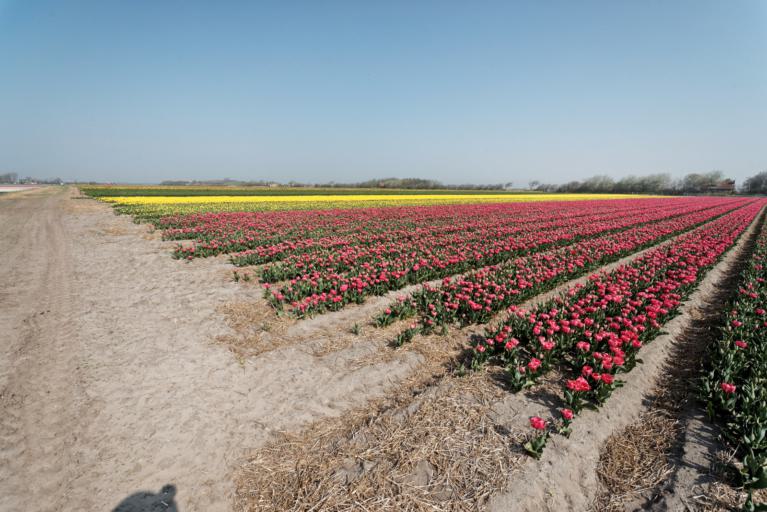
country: NL
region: North Holland
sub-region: Gemeente Texel
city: Den Burg
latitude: 53.0081
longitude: 4.7903
